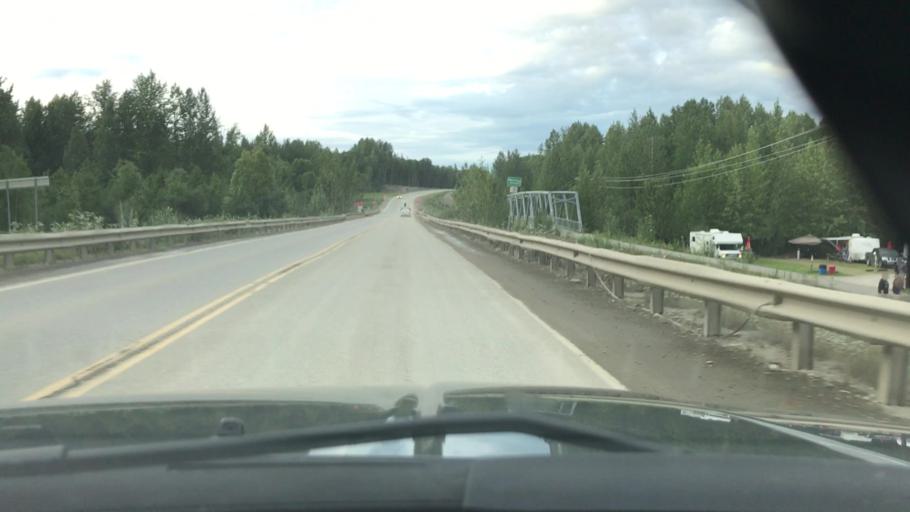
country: US
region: Alaska
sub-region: Matanuska-Susitna Borough
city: Y
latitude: 62.1034
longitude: -150.0601
